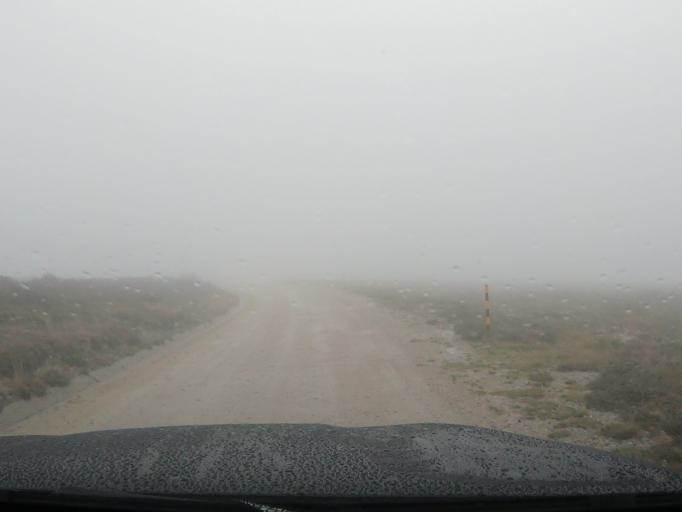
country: PT
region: Vila Real
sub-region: Vila Real
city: Vila Real
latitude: 41.3342
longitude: -7.8368
